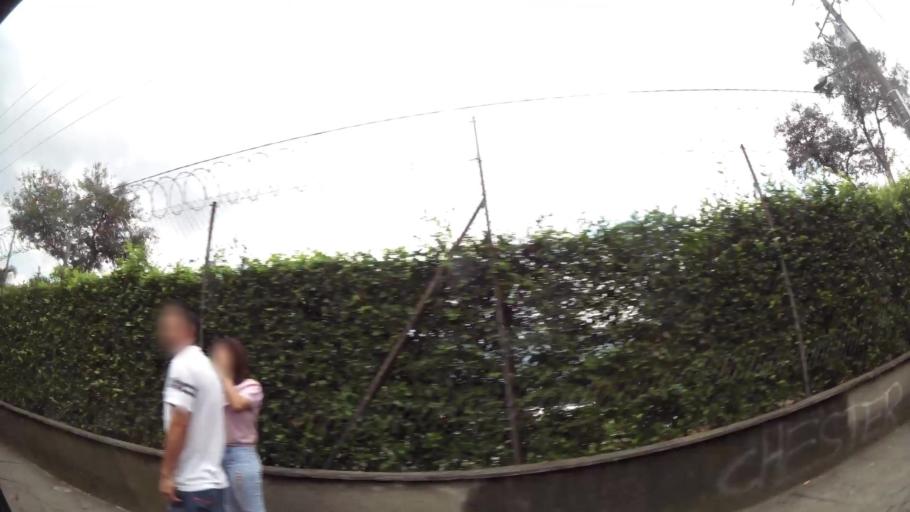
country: CO
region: Antioquia
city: Itagui
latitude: 6.1869
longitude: -75.5936
